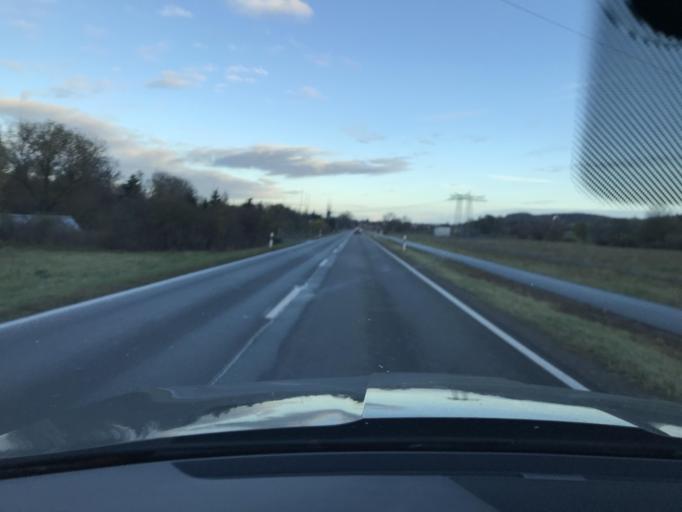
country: DE
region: Saxony-Anhalt
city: Neinstedt
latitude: 51.7522
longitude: 11.0652
